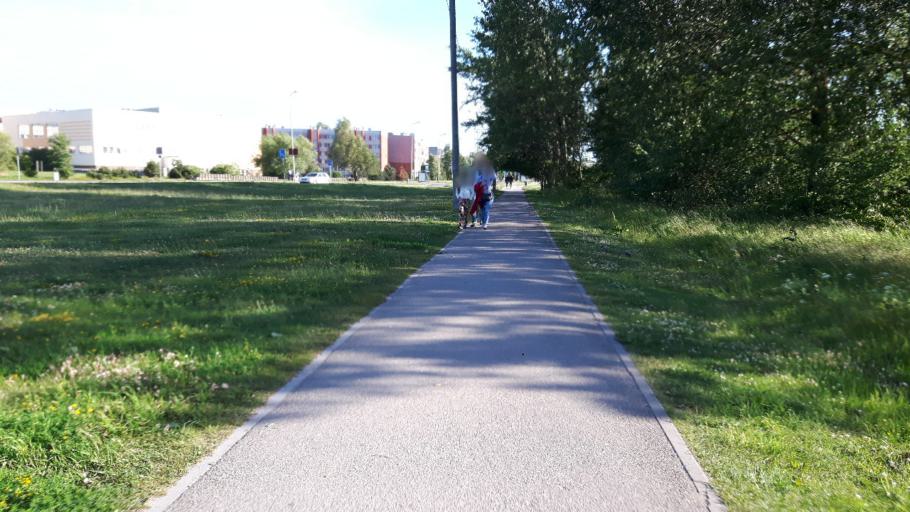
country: LV
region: Liepaja
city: Vec-Liepaja
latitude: 56.5418
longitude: 21.0037
